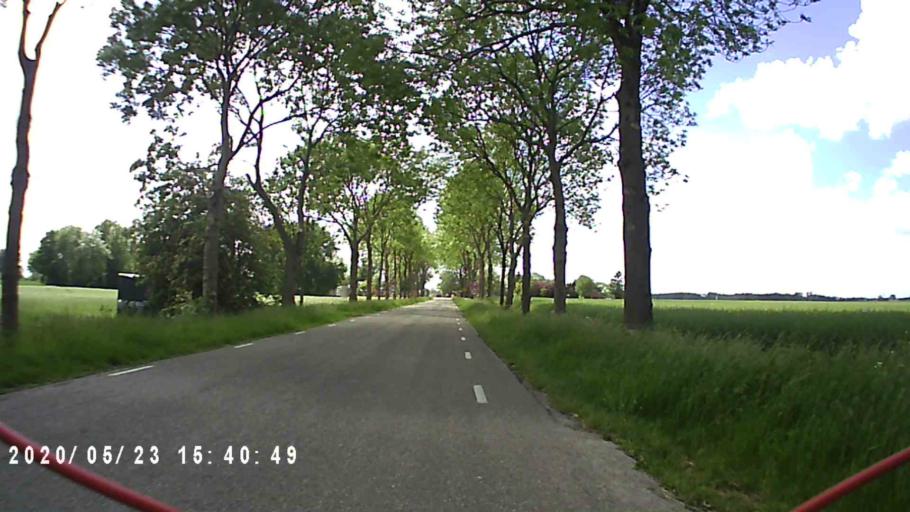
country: NL
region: Groningen
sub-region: Gemeente Delfzijl
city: Delfzijl
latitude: 53.2808
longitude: 6.9353
